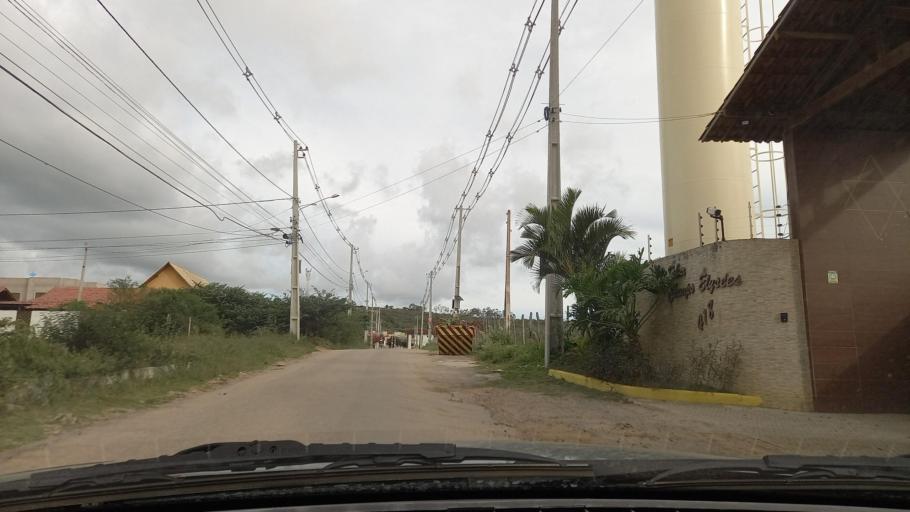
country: BR
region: Pernambuco
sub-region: Gravata
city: Gravata
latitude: -8.2006
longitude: -35.5490
